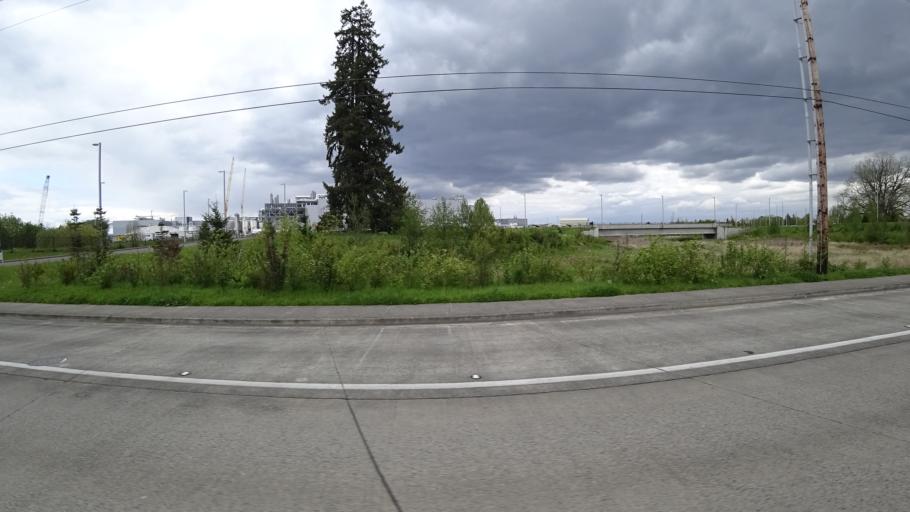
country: US
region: Oregon
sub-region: Washington County
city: Rockcreek
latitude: 45.5408
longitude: -122.9264
